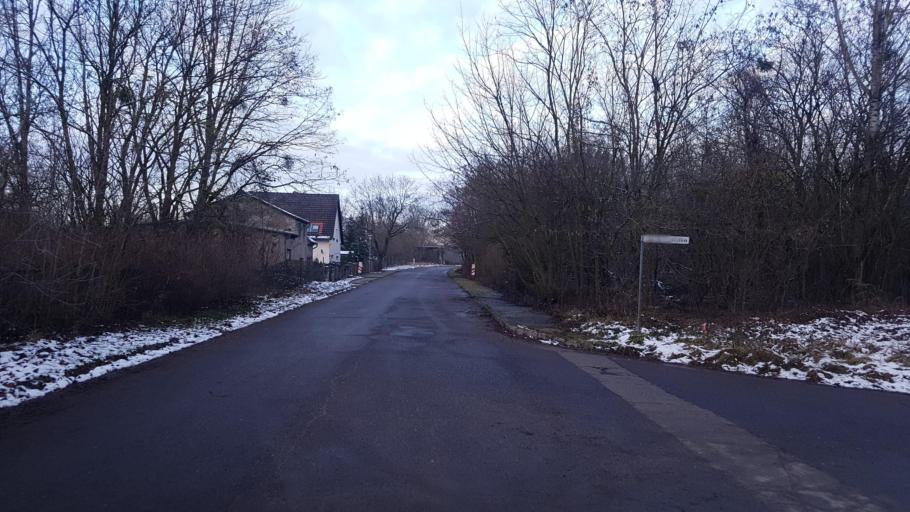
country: DE
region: Brandenburg
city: Petershagen
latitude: 52.4865
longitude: 13.7899
